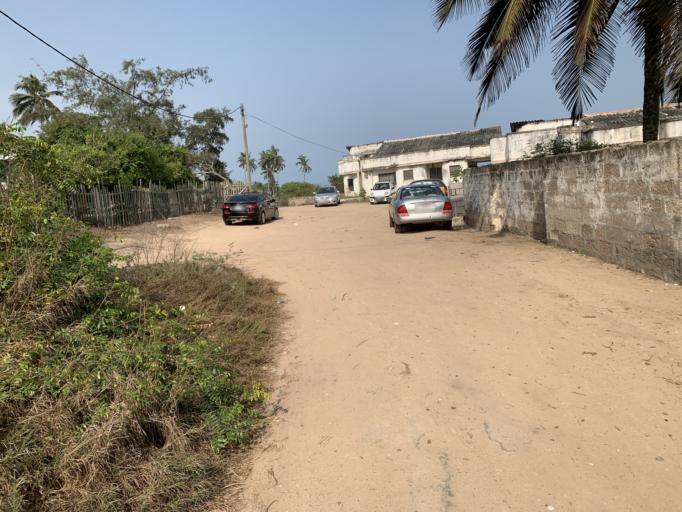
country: GH
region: Central
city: Winneba
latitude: 5.3316
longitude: -0.6257
